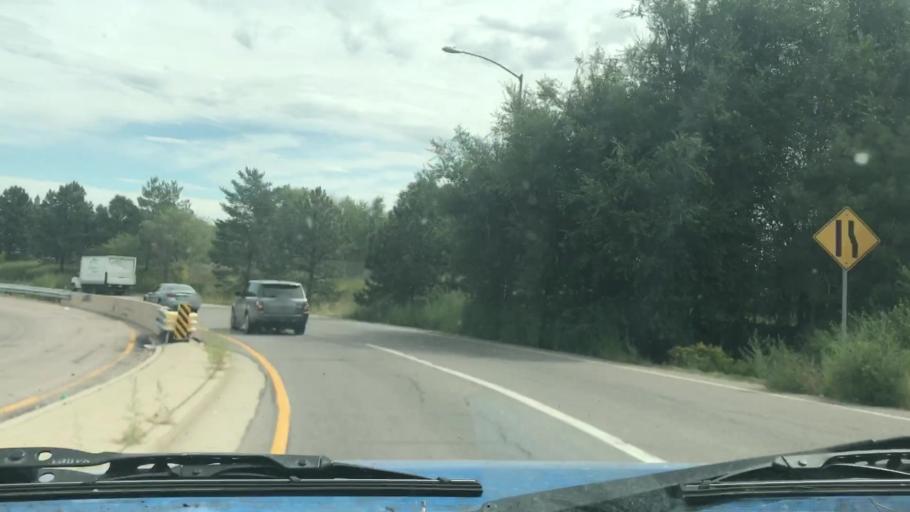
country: US
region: Colorado
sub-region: Arapahoe County
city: Sheridan
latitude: 39.6517
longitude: -105.0524
